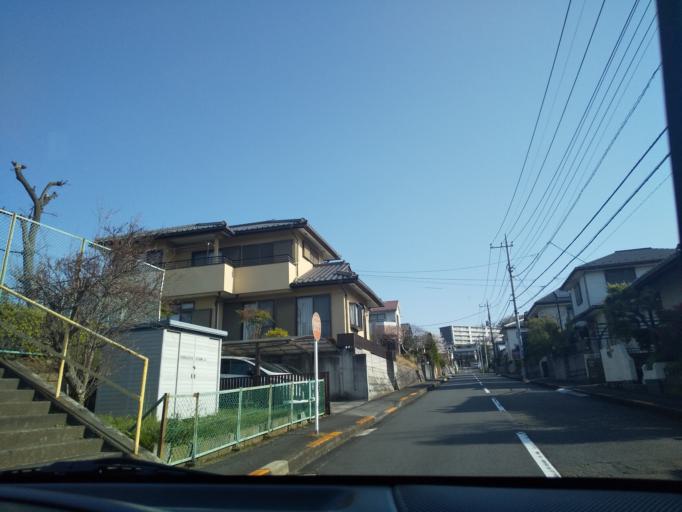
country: JP
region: Tokyo
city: Hino
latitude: 35.6507
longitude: 139.4232
